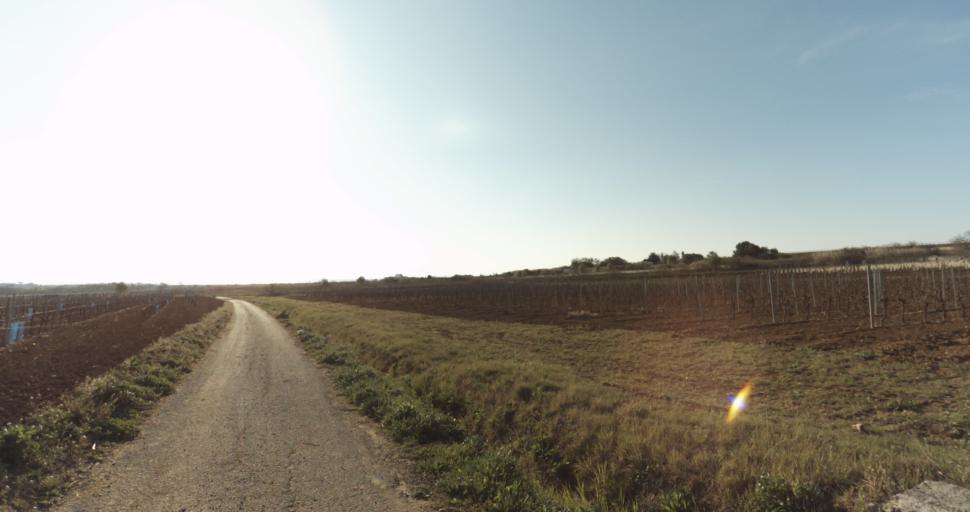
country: FR
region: Languedoc-Roussillon
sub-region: Departement de l'Herault
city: Marseillan
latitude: 43.3832
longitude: 3.5269
